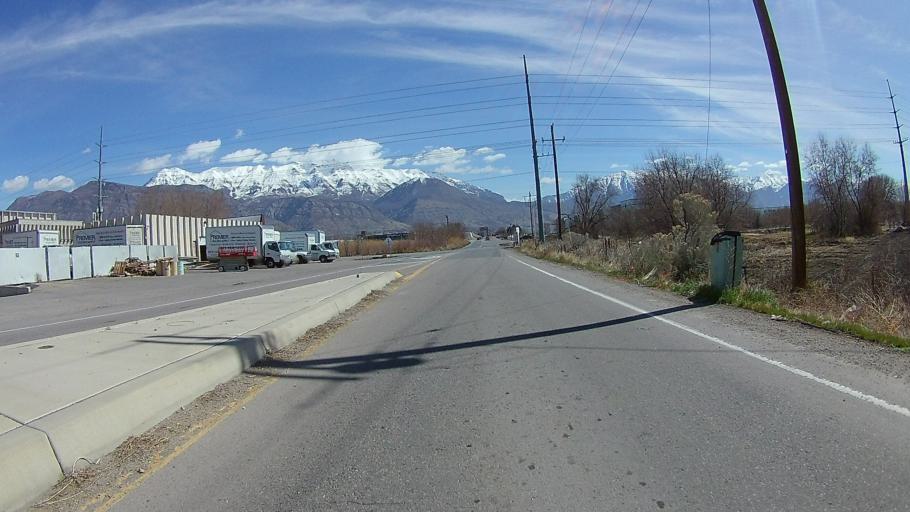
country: US
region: Utah
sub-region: Utah County
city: American Fork
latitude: 40.3550
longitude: -111.7866
